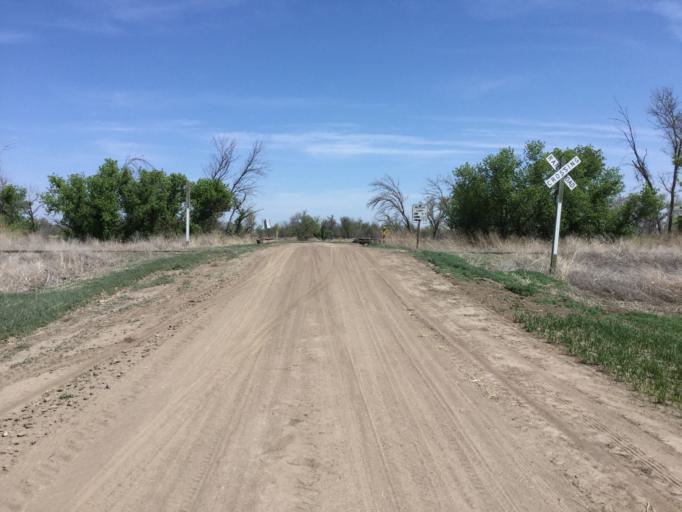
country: US
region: Kansas
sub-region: Decatur County
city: Oberlin
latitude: 39.9130
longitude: -100.7028
